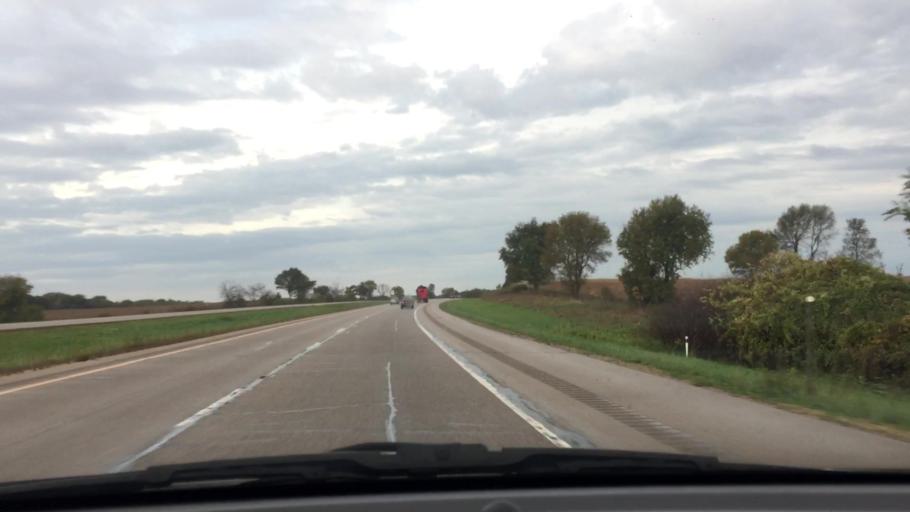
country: US
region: Wisconsin
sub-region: Rock County
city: Clinton
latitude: 42.5730
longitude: -88.8079
